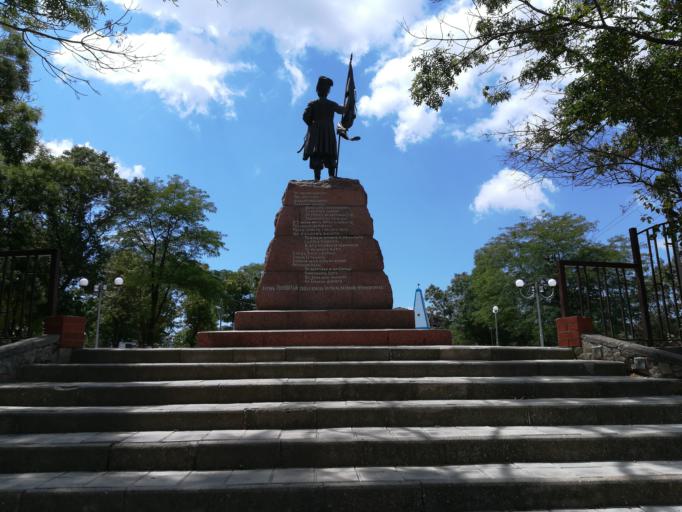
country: RU
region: Krasnodarskiy
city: Taman'
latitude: 45.2180
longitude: 36.7218
